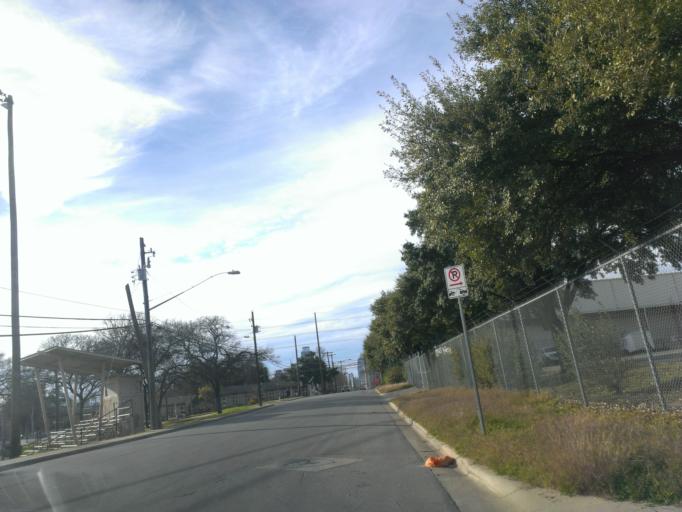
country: US
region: Texas
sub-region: Travis County
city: Austin
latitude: 30.2594
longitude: -97.7222
